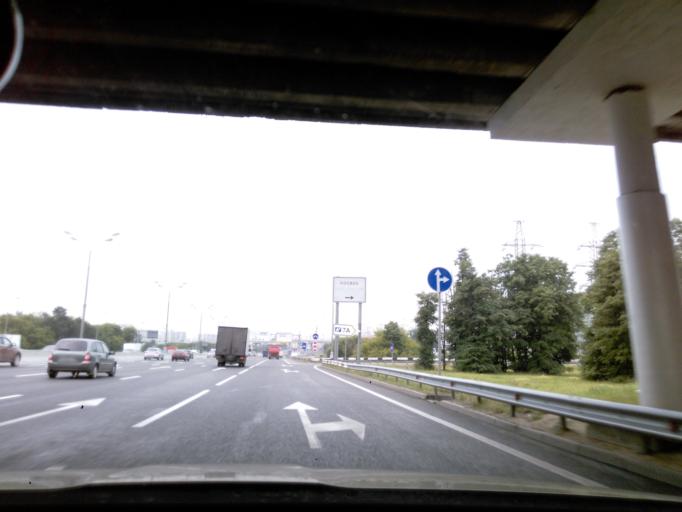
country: RU
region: Moscow
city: Veshnyaki
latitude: 55.7187
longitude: 37.8386
